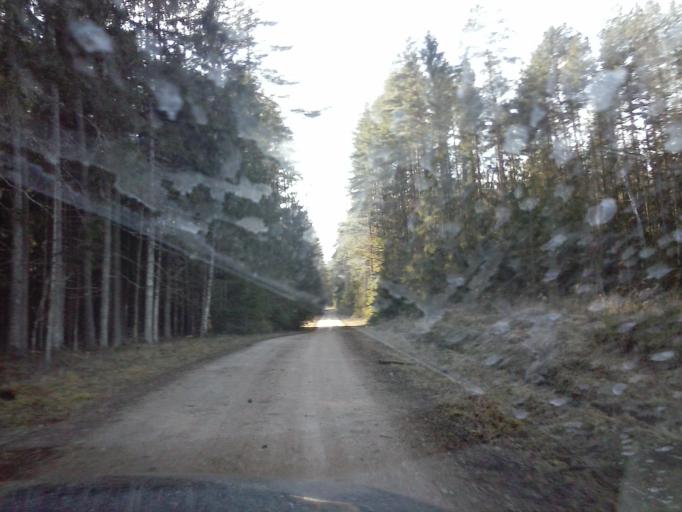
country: EE
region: Tartu
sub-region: Puhja vald
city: Puhja
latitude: 58.1587
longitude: 26.1448
